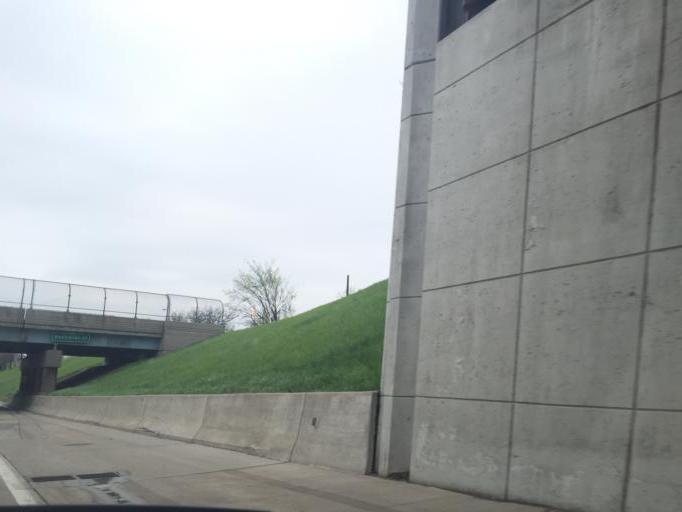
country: US
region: Michigan
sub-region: Wayne County
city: Detroit
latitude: 42.3424
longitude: -83.0946
